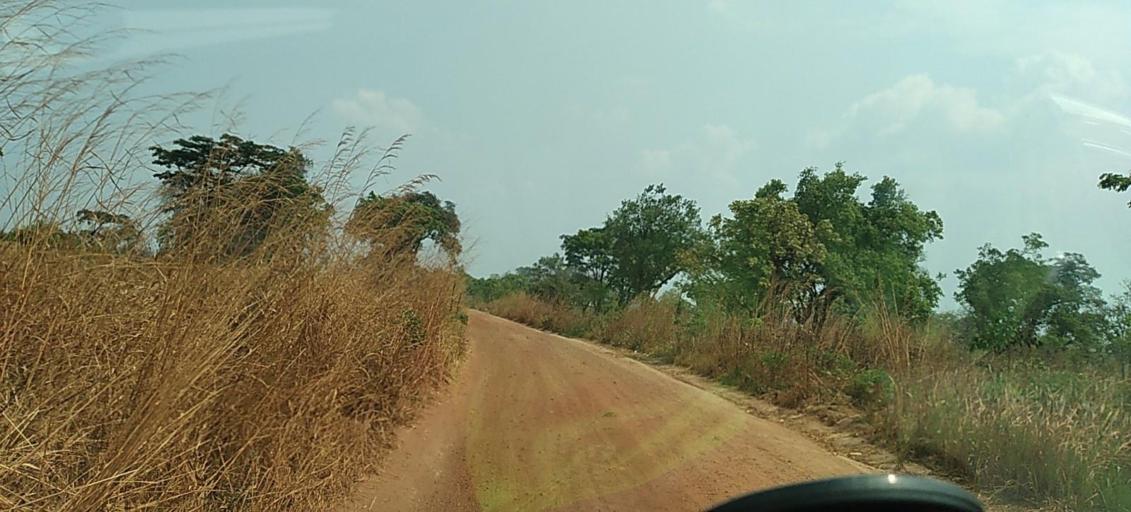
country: ZM
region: North-Western
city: Kansanshi
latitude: -12.0898
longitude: 26.3658
